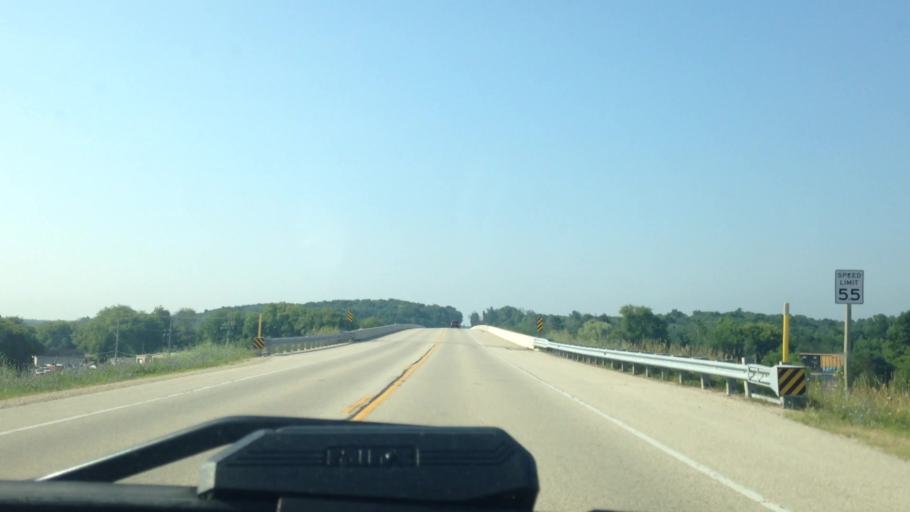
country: US
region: Wisconsin
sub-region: Washington County
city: Slinger
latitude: 43.3129
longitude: -88.2609
